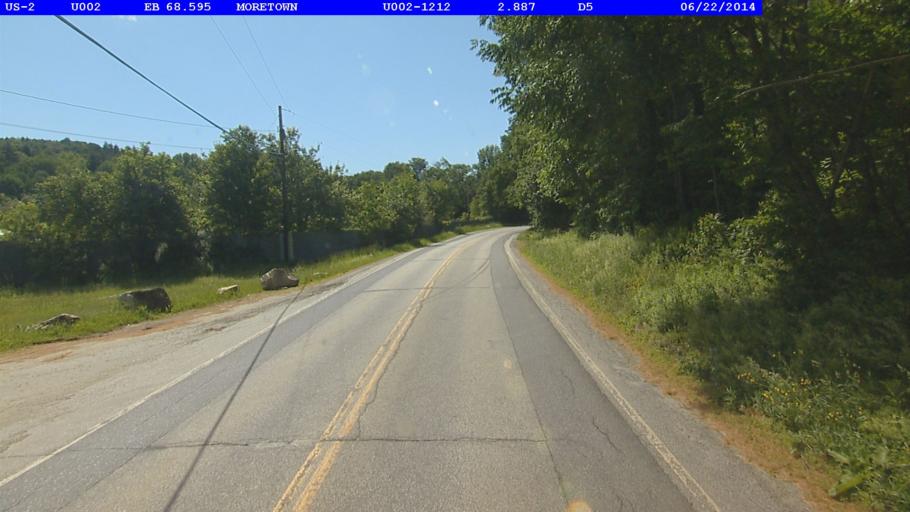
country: US
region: Vermont
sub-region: Washington County
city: Waterbury
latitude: 44.3106
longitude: -72.6985
